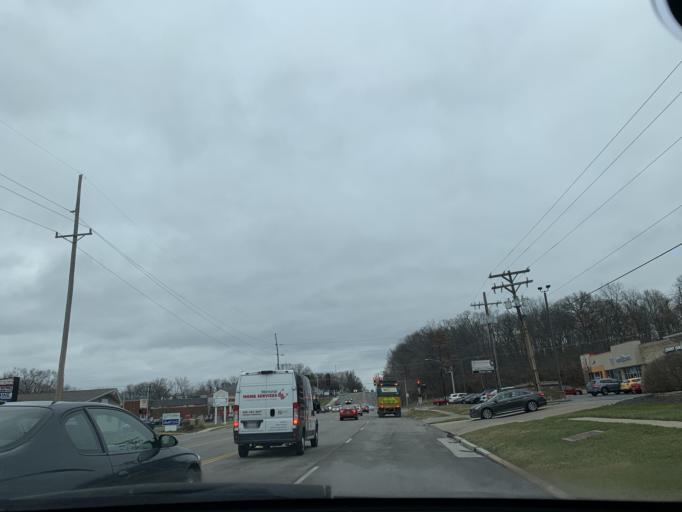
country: US
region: Illinois
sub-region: Sangamon County
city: Leland Grove
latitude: 39.8003
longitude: -89.6869
